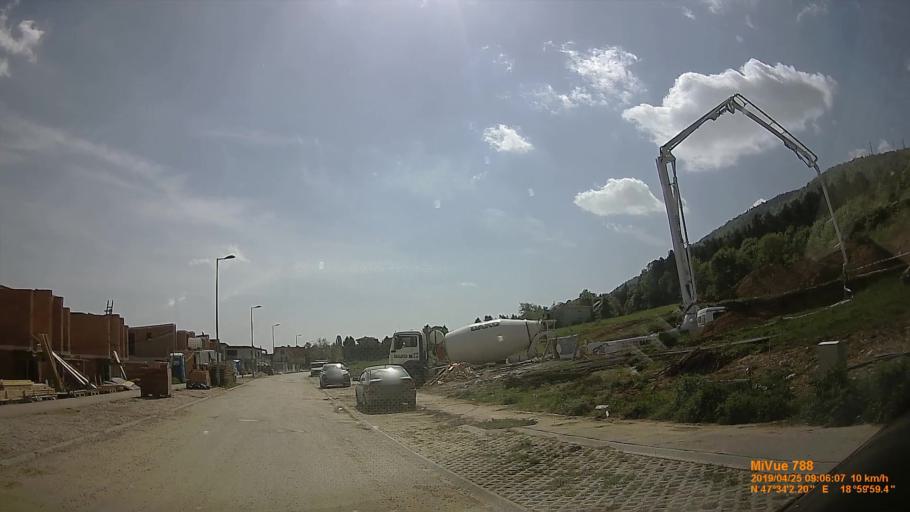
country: HU
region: Pest
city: Urom
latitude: 47.5673
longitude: 18.9999
